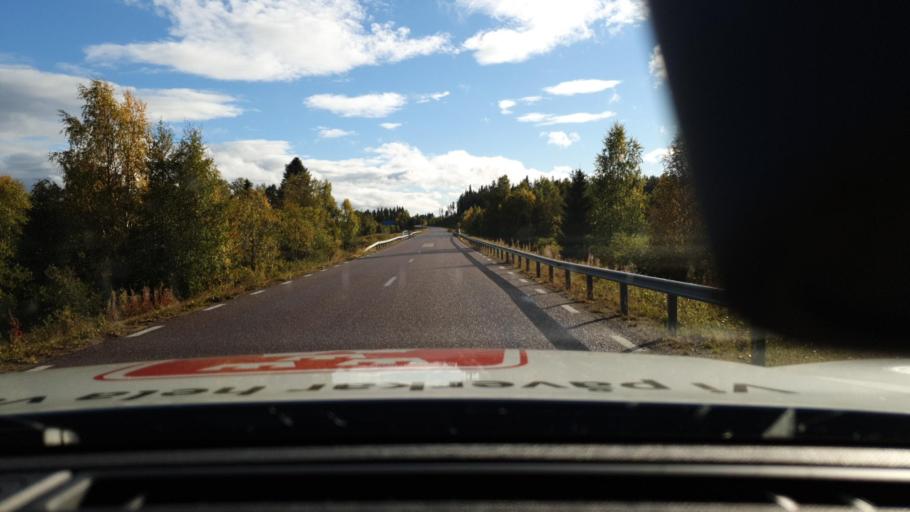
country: SE
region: Norrbotten
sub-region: Overkalix Kommun
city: OEverkalix
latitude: 66.7759
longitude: 22.6954
